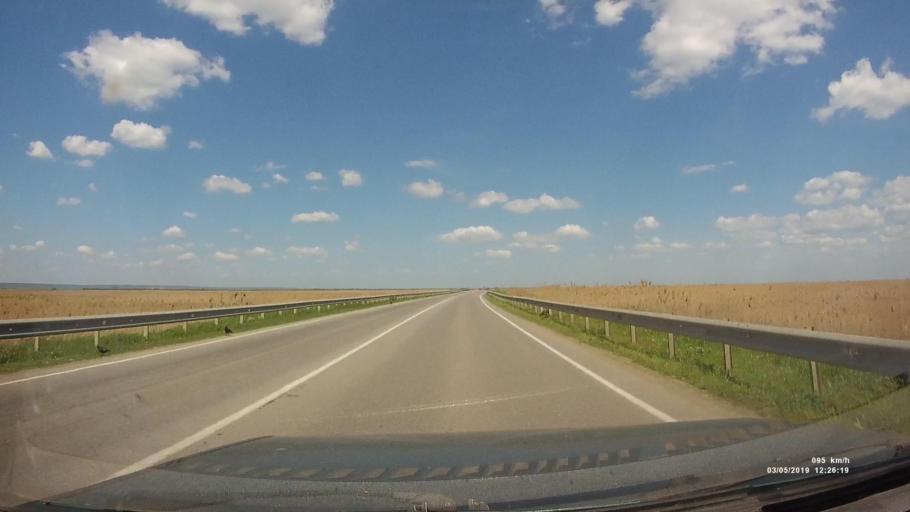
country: RU
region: Rostov
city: Semikarakorsk
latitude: 47.4435
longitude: 40.7129
